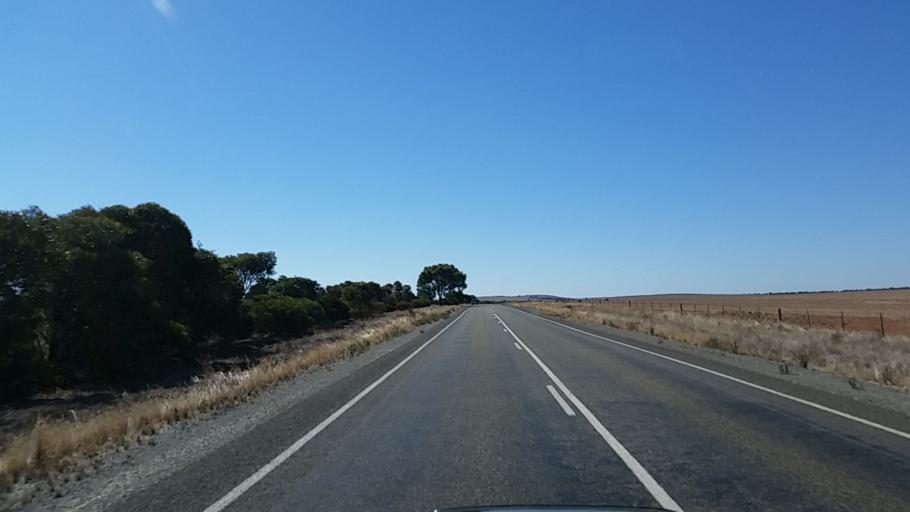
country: AU
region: South Australia
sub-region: Northern Areas
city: Jamestown
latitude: -33.2587
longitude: 138.8706
